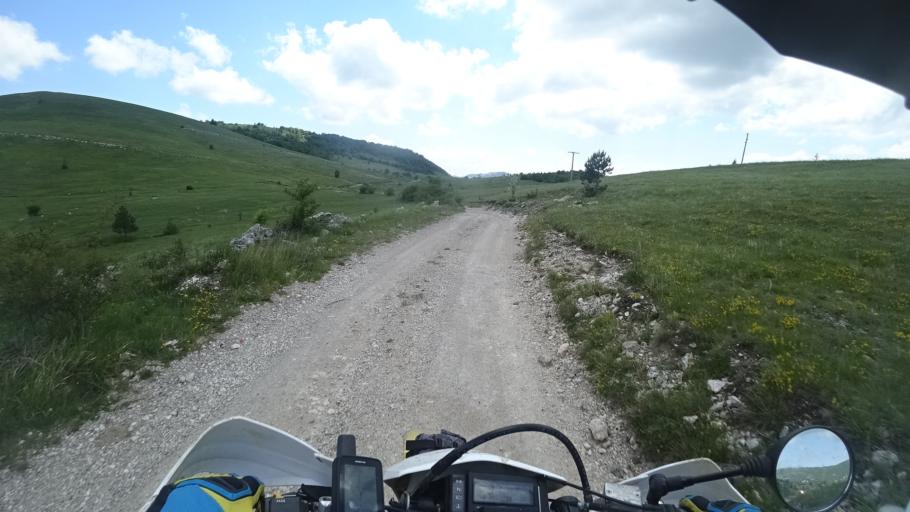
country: HR
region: Zadarska
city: Gracac
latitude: 44.2985
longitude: 15.9460
